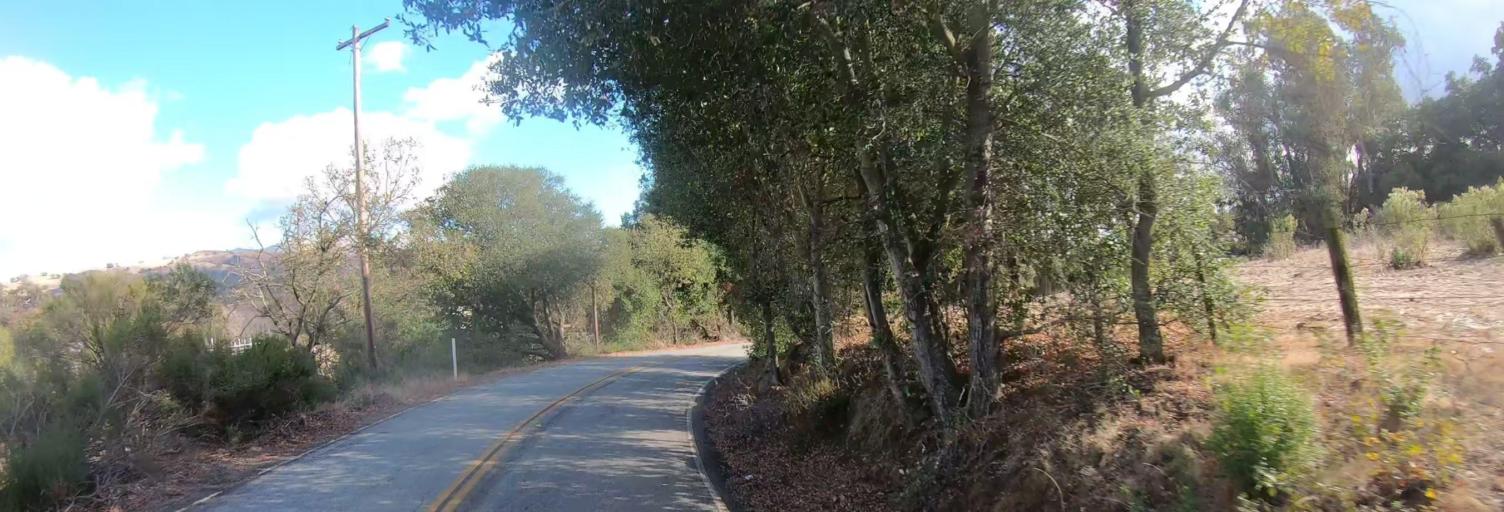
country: US
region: California
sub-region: Santa Clara County
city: East Foothills
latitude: 37.3463
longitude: -121.7263
